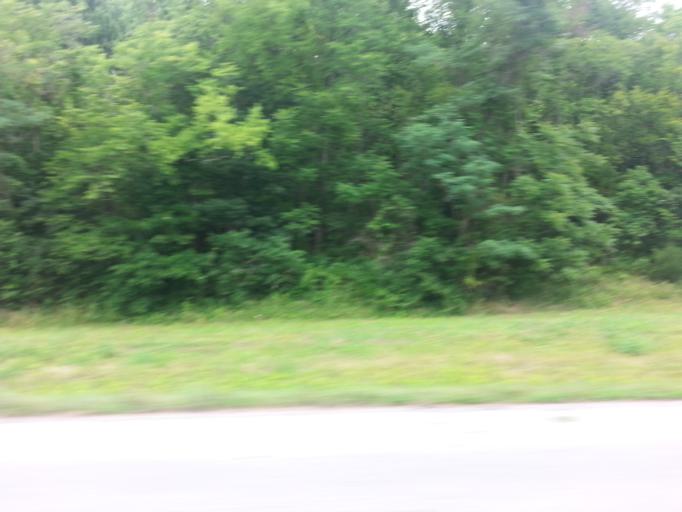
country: US
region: Ohio
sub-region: Brown County
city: Aberdeen
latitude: 38.7018
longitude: -83.7880
